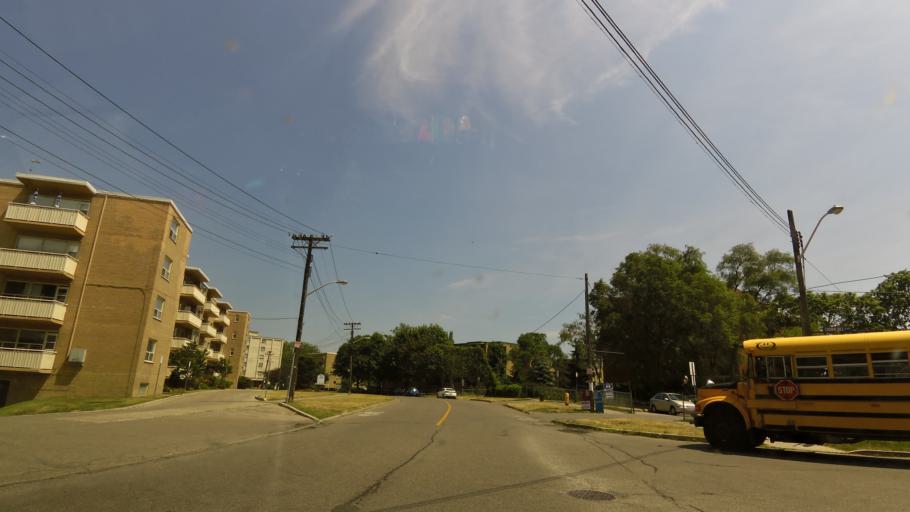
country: CA
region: Ontario
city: Etobicoke
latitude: 43.6398
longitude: -79.4897
